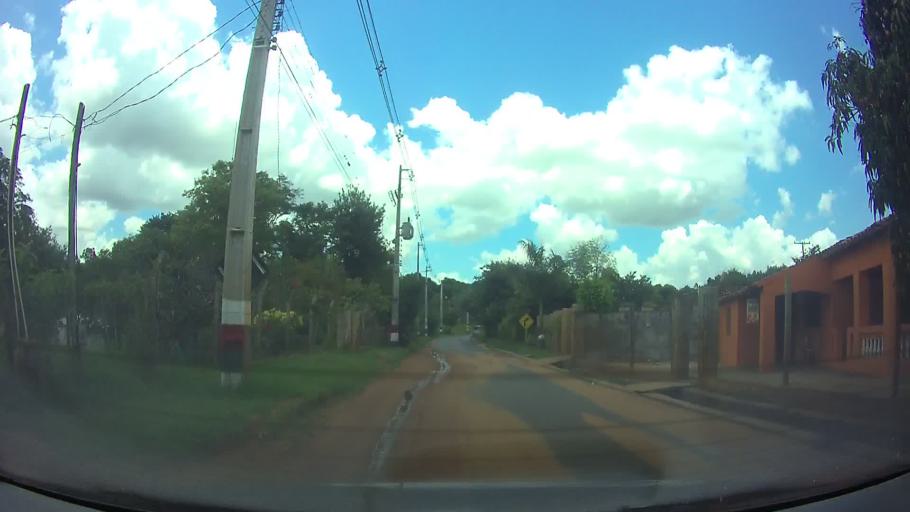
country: PY
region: Central
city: Capiata
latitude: -25.3410
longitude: -57.4189
